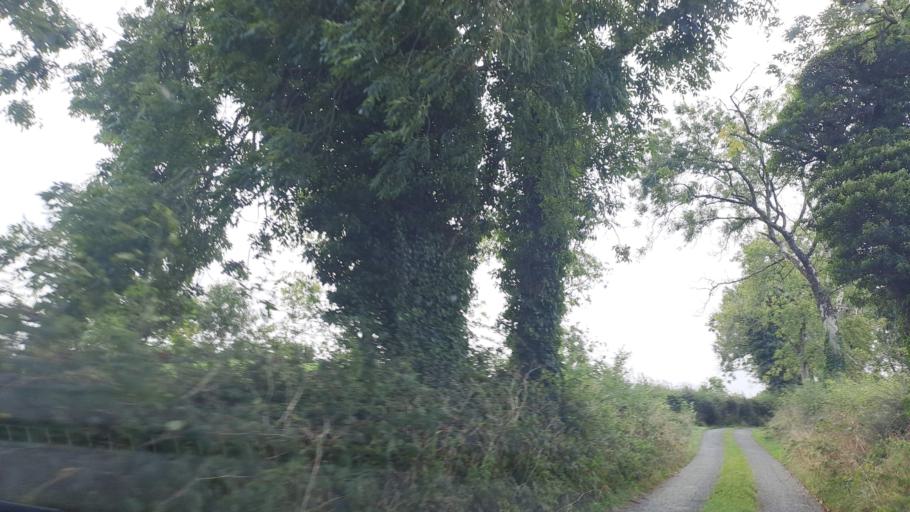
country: IE
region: Ulster
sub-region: An Cabhan
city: Kingscourt
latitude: 53.9887
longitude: -6.8317
